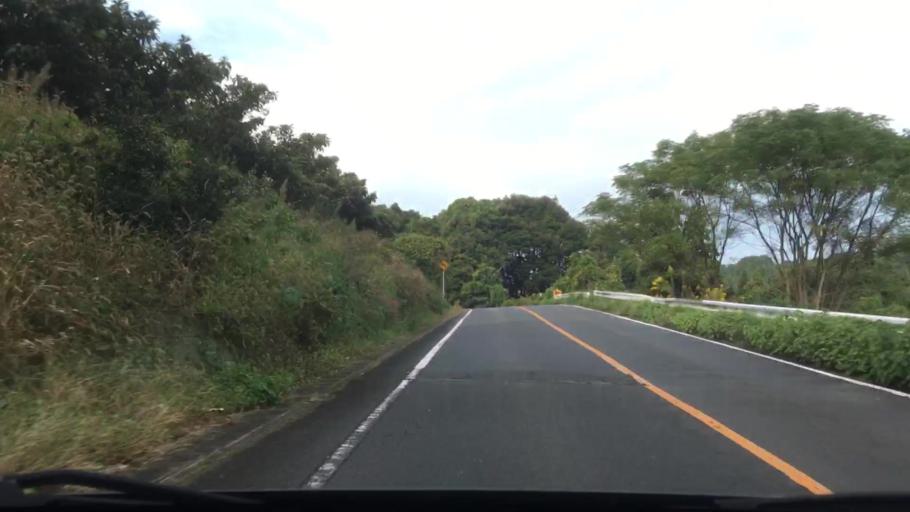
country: JP
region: Nagasaki
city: Sasebo
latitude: 33.0390
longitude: 129.6868
